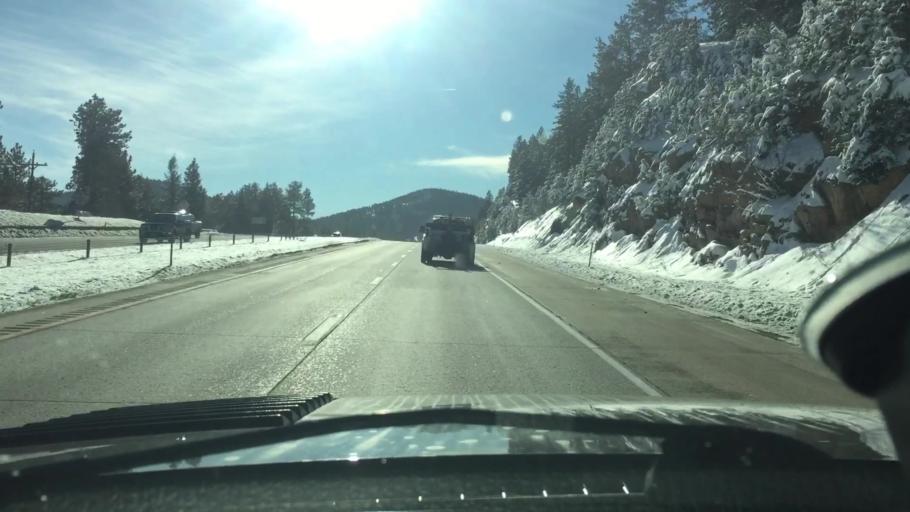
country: US
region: Colorado
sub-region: Jefferson County
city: Indian Hills
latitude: 39.6010
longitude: -105.2283
